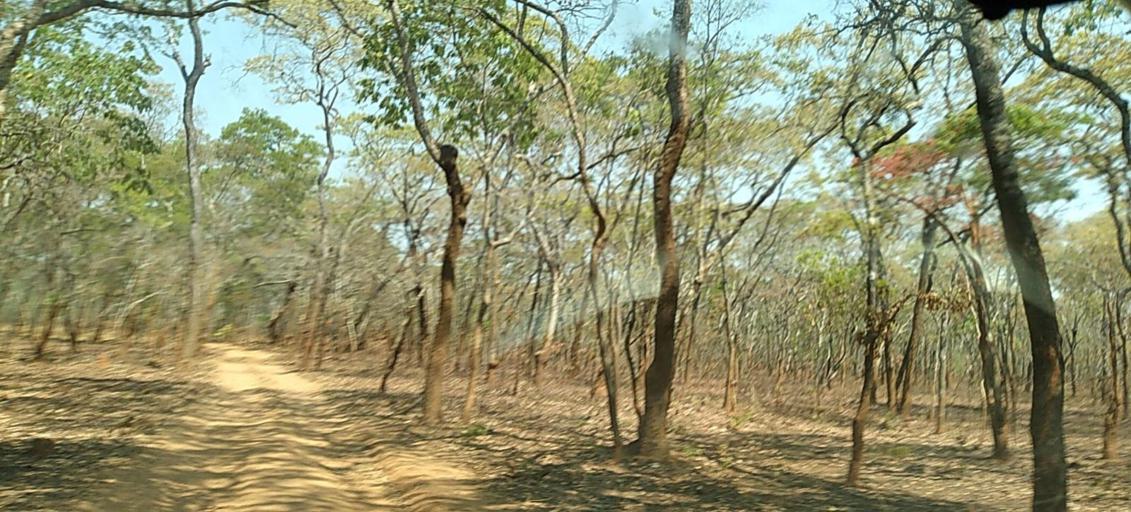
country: ZM
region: North-Western
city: Kasempa
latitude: -13.3936
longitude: 25.5928
